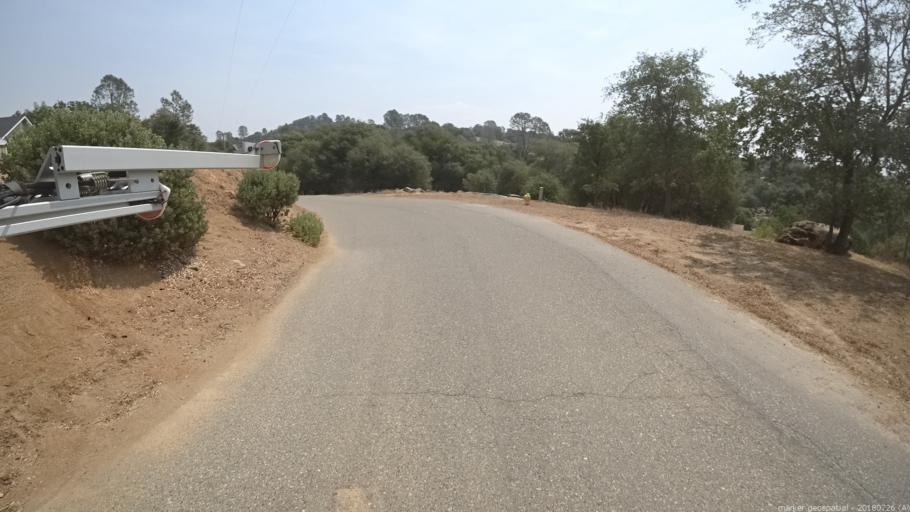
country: US
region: California
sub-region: Madera County
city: Coarsegold
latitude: 37.2527
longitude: -119.6897
